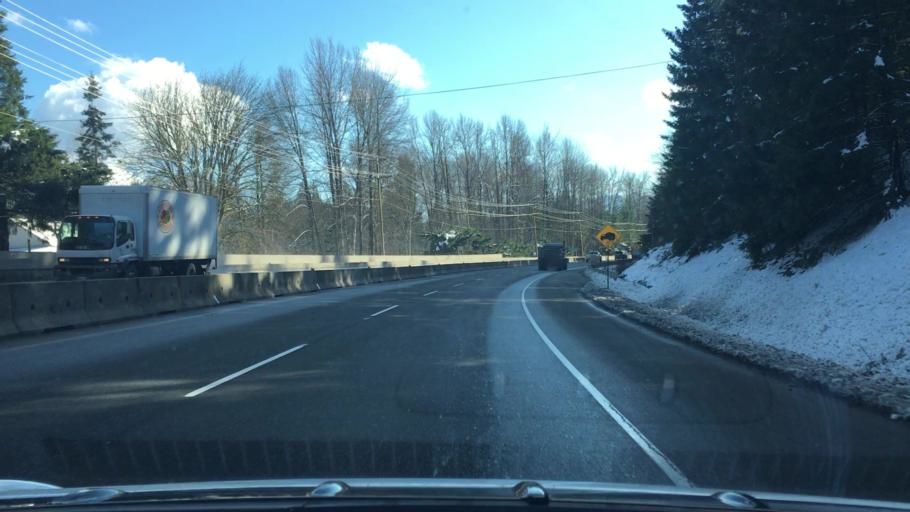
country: CA
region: British Columbia
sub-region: Cowichan Valley Regional District
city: Ladysmith
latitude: 49.0658
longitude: -123.8773
